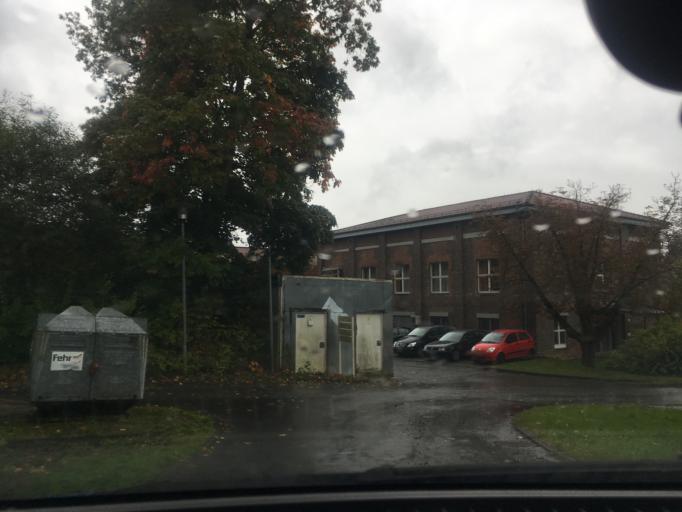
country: DE
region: Lower Saxony
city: Bodenfelde
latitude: 51.6172
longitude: 9.5920
